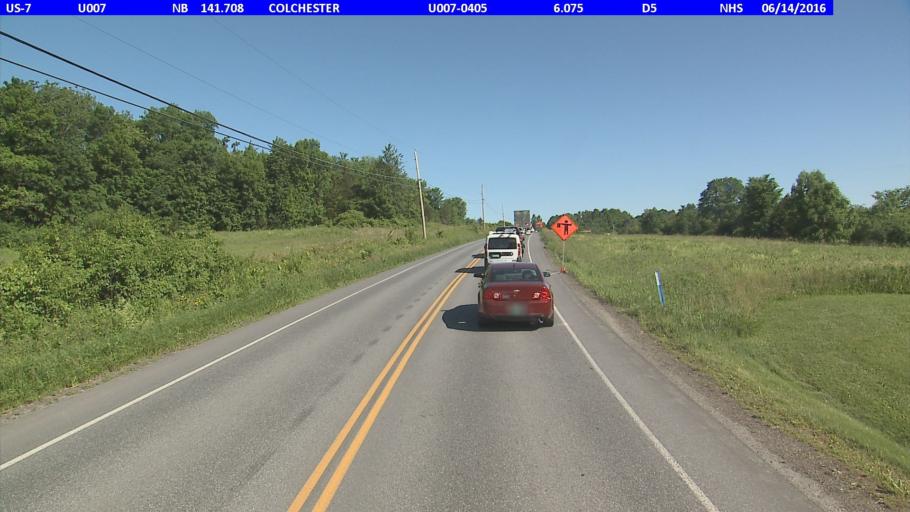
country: US
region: Vermont
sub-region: Chittenden County
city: Colchester
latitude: 44.5833
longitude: -73.1645
